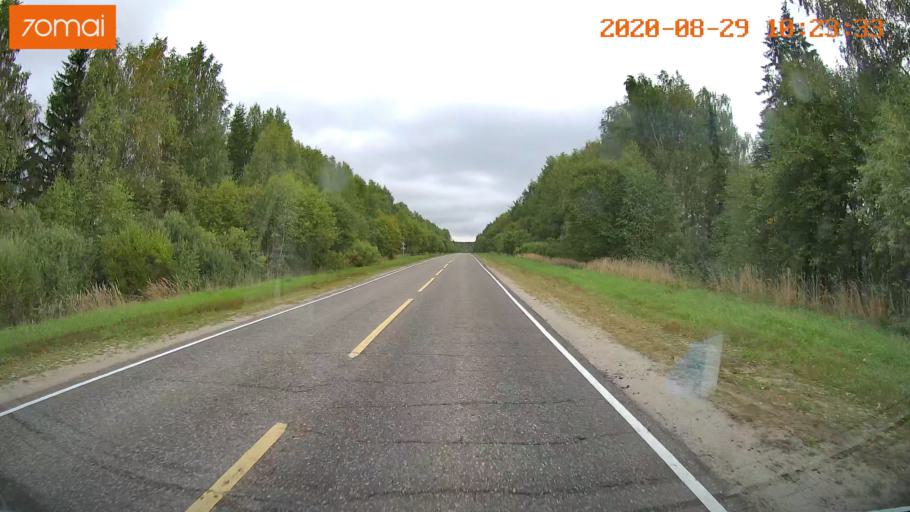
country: RU
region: Ivanovo
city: Yur'yevets
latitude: 57.3235
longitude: 42.9762
